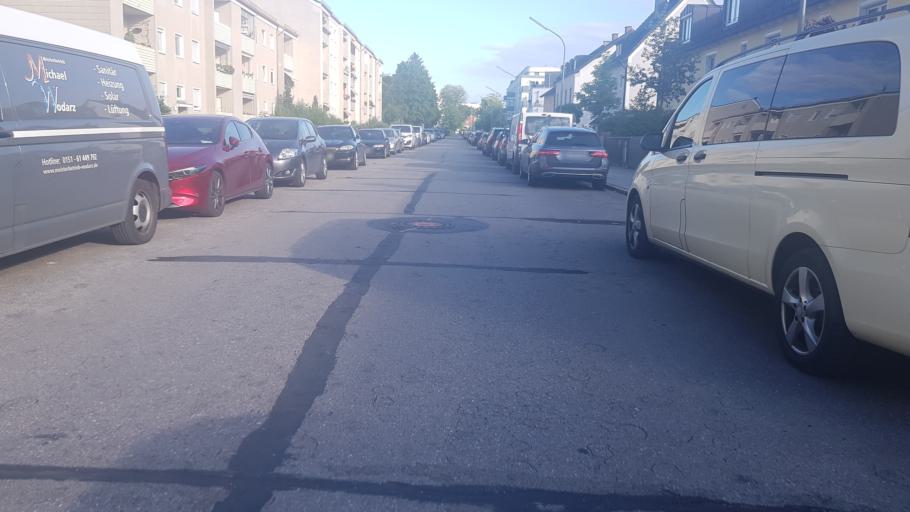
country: DE
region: Bavaria
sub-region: Upper Bavaria
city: Pasing
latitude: 48.1496
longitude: 11.4498
